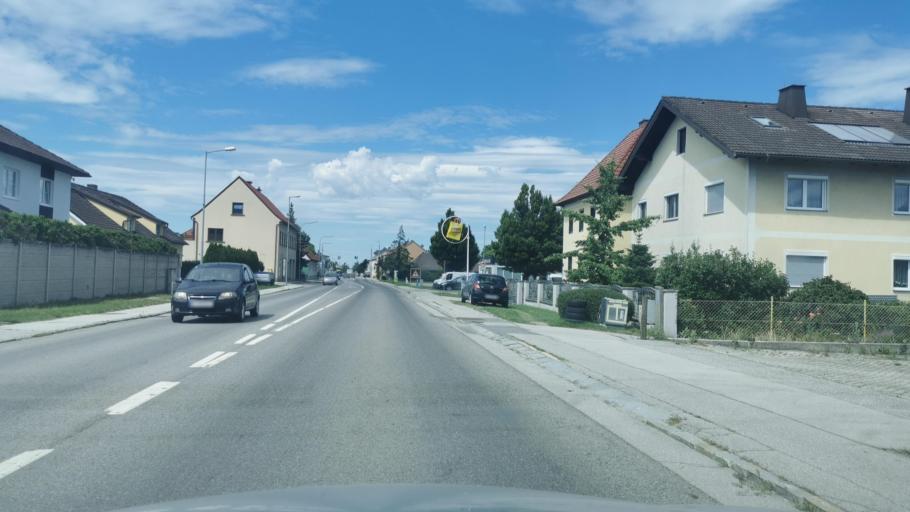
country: AT
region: Lower Austria
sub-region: Politischer Bezirk Sankt Polten
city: Wilhelmsburg
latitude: 48.1365
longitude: 15.6132
